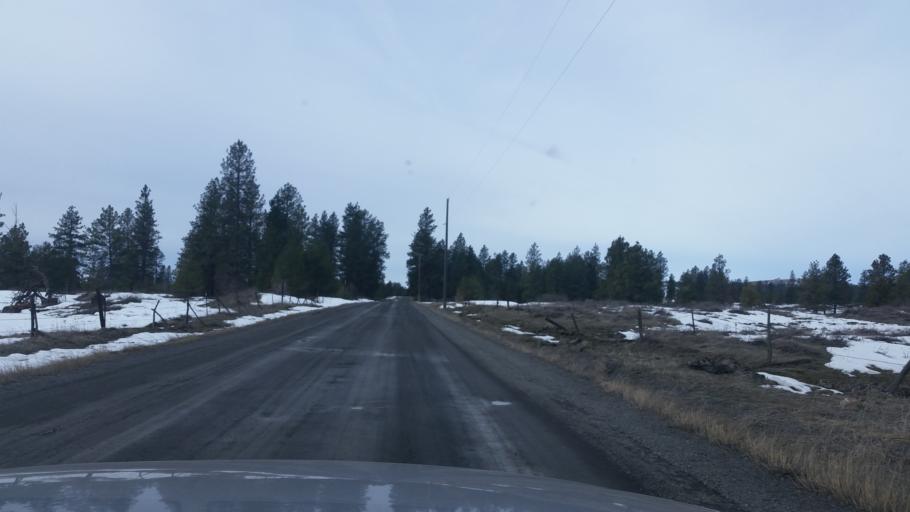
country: US
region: Washington
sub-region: Spokane County
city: Fairchild Air Force Base
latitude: 47.5801
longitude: -117.6346
